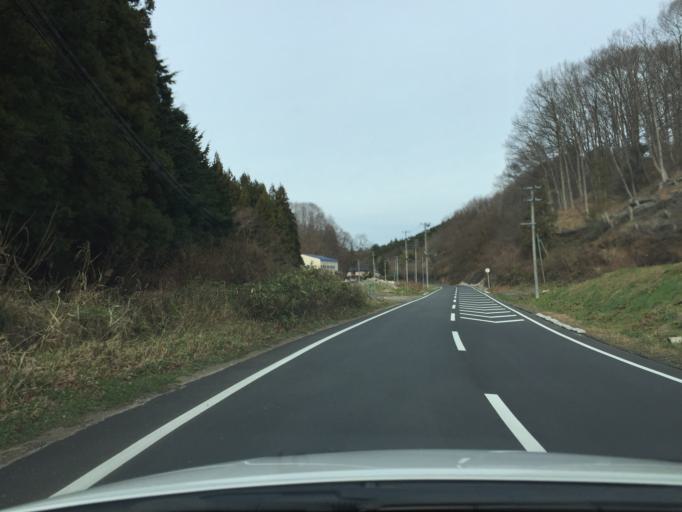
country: JP
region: Fukushima
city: Ishikawa
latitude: 37.2332
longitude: 140.6291
